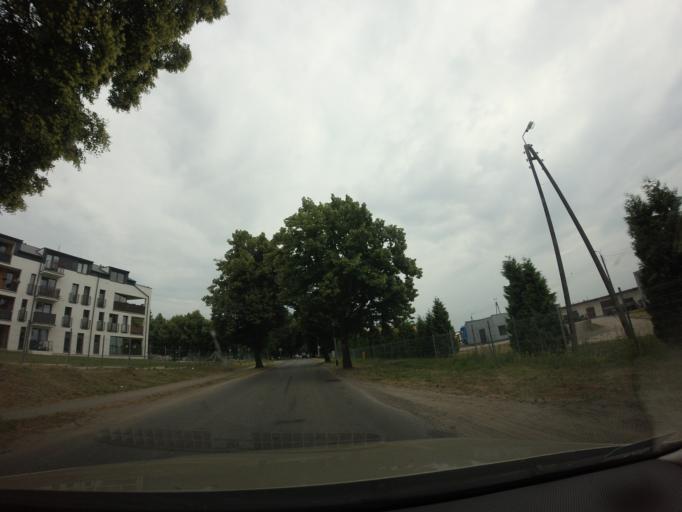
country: PL
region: West Pomeranian Voivodeship
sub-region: Powiat drawski
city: Czaplinek
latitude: 53.5482
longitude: 16.2322
